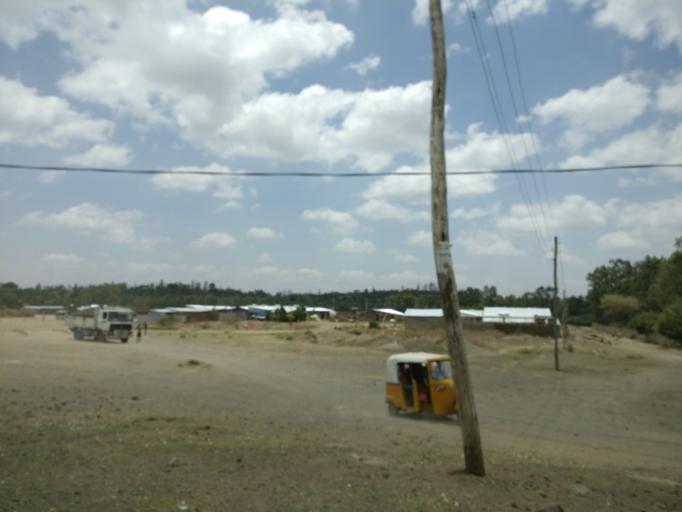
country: ET
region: Oromiya
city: Bishoftu
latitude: 8.7756
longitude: 38.9869
